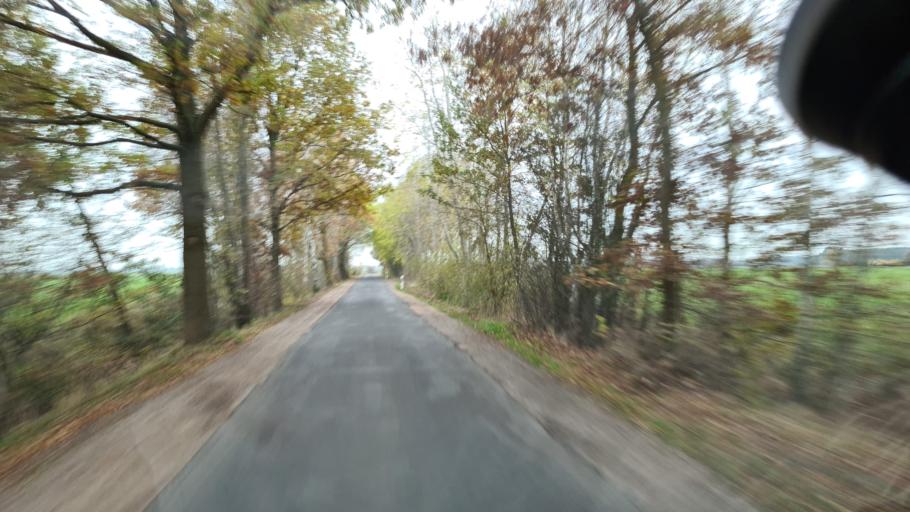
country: DE
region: Brandenburg
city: Ruthnick
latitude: 52.9219
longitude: 12.9958
